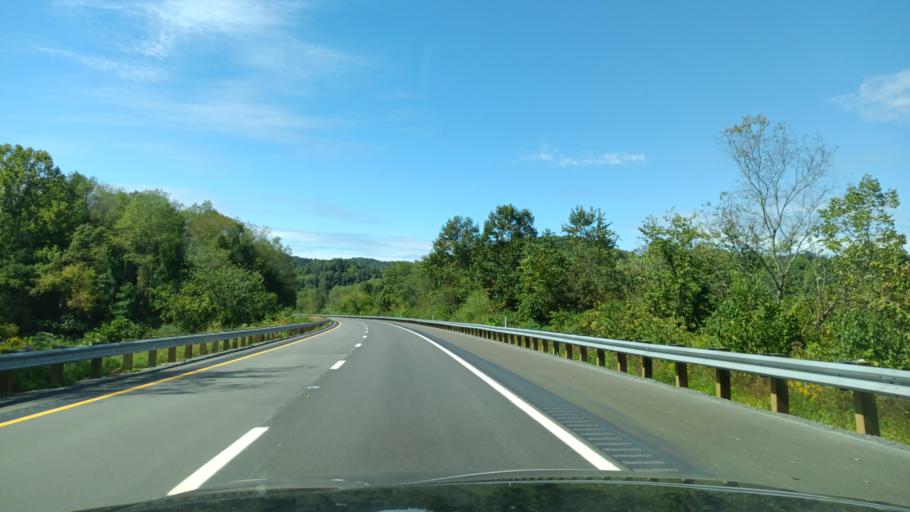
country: US
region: West Virginia
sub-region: Harrison County
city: Clarksburg
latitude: 39.2872
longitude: -80.4314
